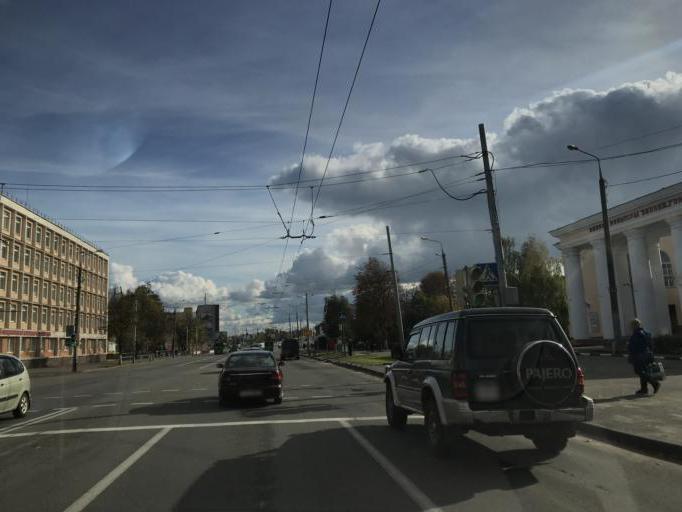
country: BY
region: Gomel
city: Gomel
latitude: 52.4489
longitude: 30.9684
